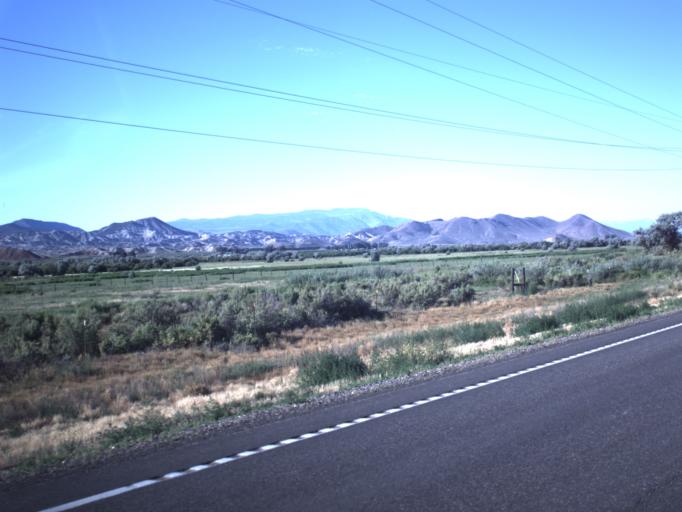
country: US
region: Utah
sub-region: Sevier County
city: Salina
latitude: 38.9361
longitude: -111.8944
